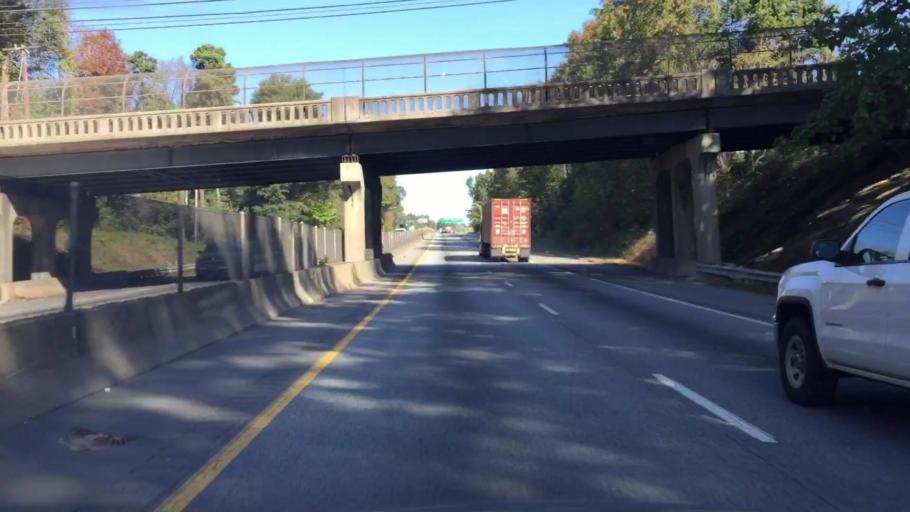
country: US
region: North Carolina
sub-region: Guilford County
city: Greensboro
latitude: 36.0572
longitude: -79.7679
